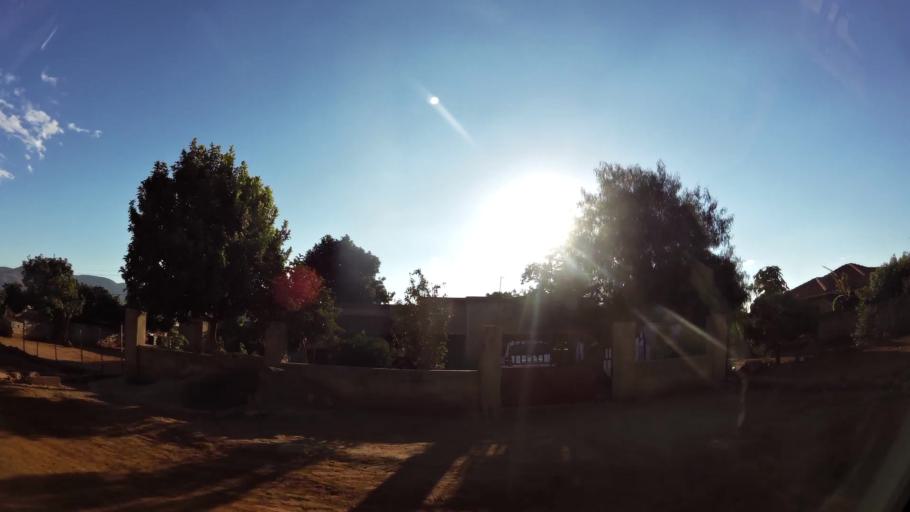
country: ZA
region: Limpopo
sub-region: Waterberg District Municipality
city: Mokopane
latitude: -24.1579
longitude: 28.9913
